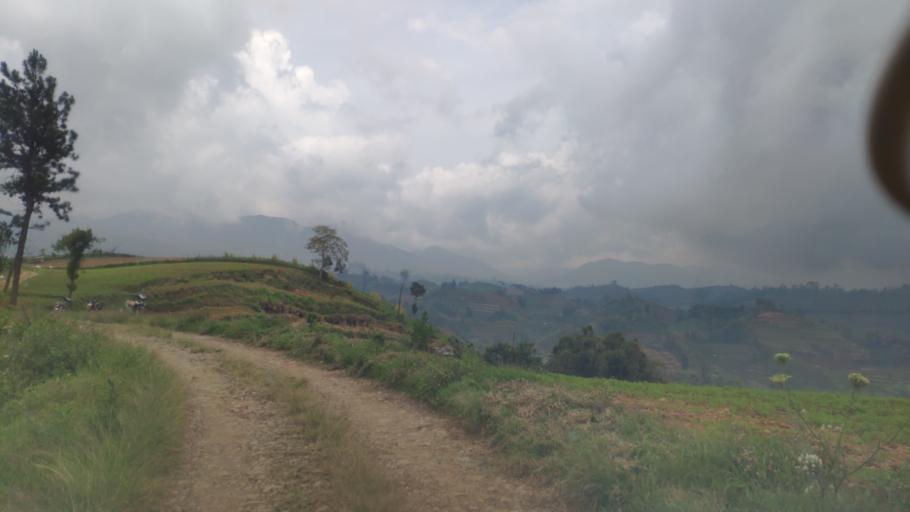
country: ID
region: Central Java
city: Wonosobo
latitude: -7.2224
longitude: 109.7868
